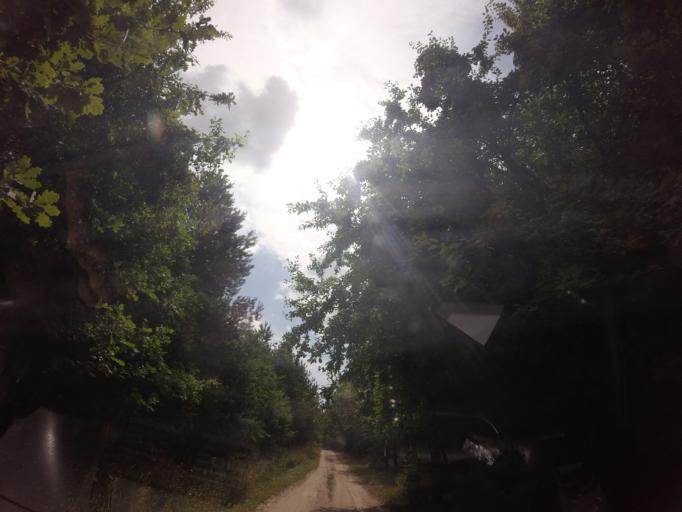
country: PL
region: West Pomeranian Voivodeship
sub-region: Powiat choszczenski
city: Drawno
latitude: 53.1990
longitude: 15.7692
